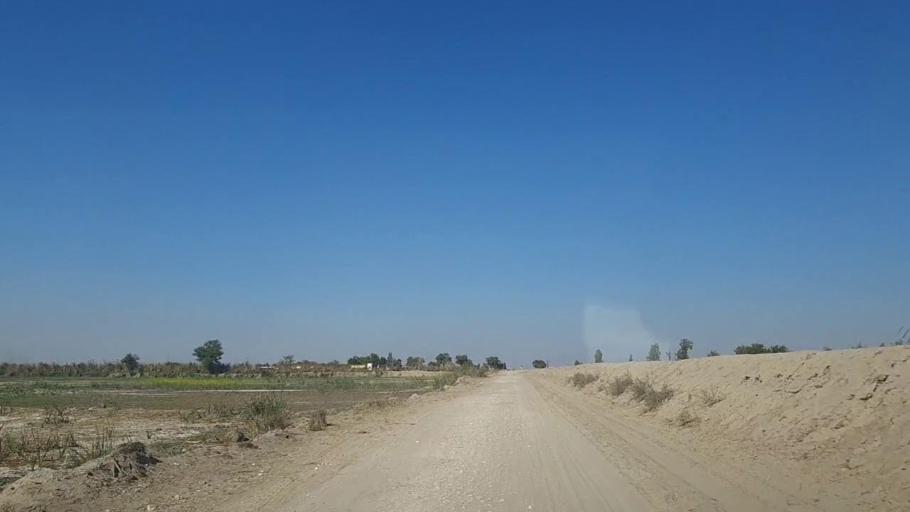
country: PK
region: Sindh
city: Sanghar
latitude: 26.2191
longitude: 68.9291
